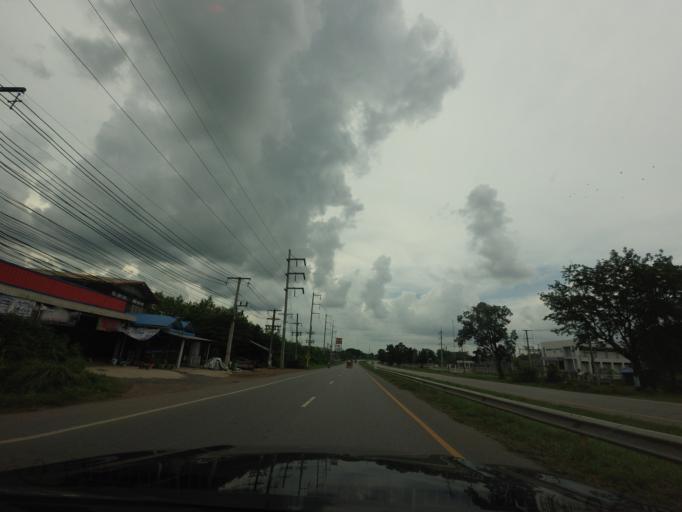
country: TH
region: Changwat Nong Bua Lamphu
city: Nong Bua Lamphu
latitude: 17.2287
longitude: 102.4050
